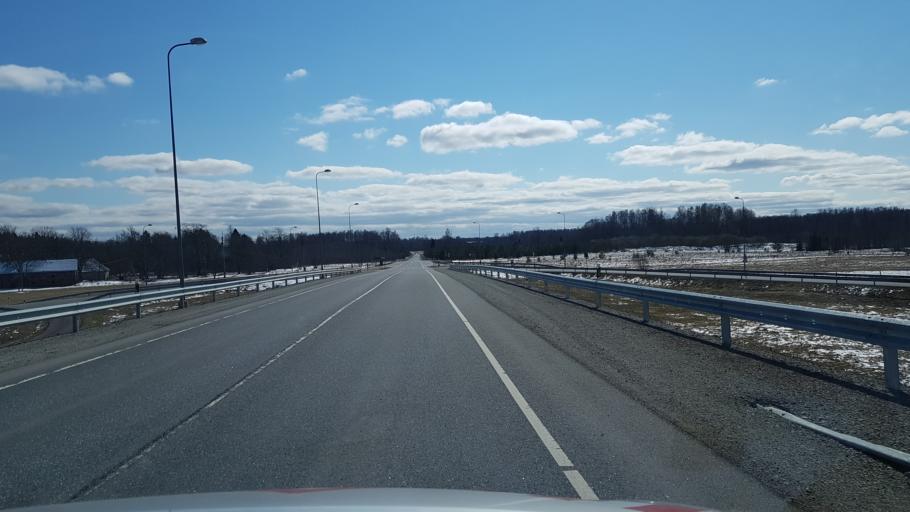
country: EE
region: Laeaene-Virumaa
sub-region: Tapa vald
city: Tapa
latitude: 59.4543
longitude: 25.9431
